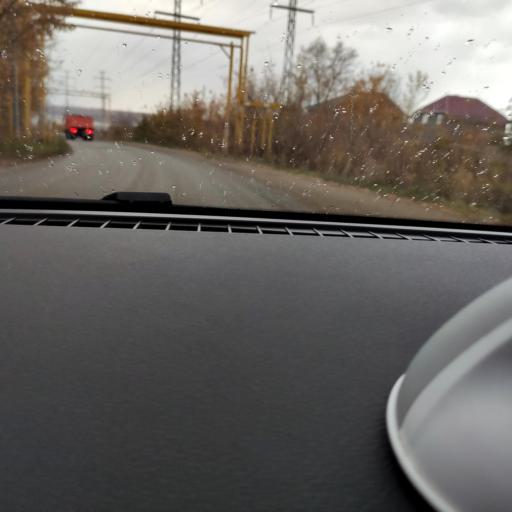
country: RU
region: Samara
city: Petra-Dubrava
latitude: 53.2944
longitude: 50.2931
